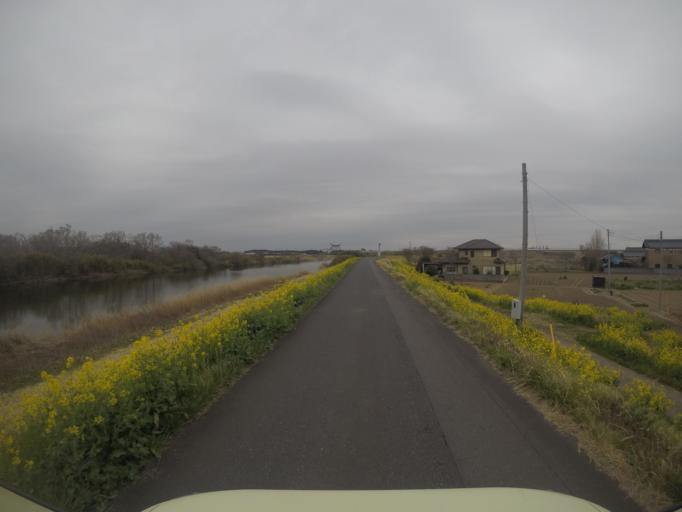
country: JP
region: Ibaraki
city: Ishige
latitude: 36.0841
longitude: 140.0000
